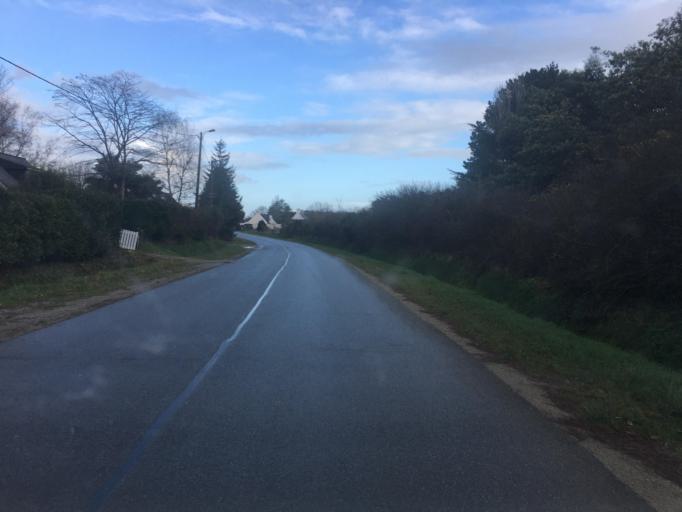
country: FR
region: Brittany
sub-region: Departement du Morbihan
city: Surzur
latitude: 47.5193
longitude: -2.6608
